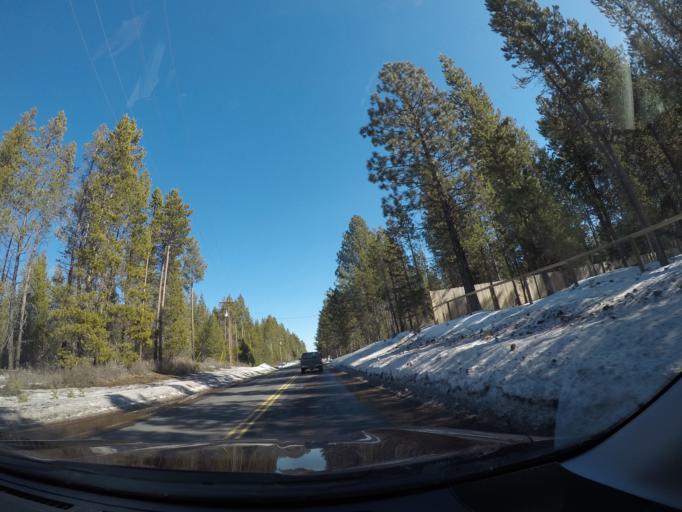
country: US
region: Oregon
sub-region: Deschutes County
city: Three Rivers
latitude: 43.8628
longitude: -121.4787
